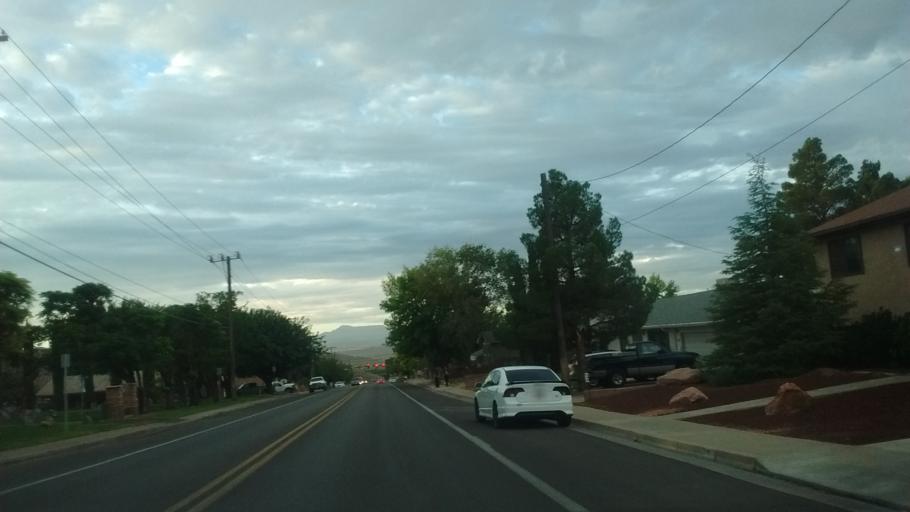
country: US
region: Utah
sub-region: Washington County
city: Washington
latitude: 37.1328
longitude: -113.5049
